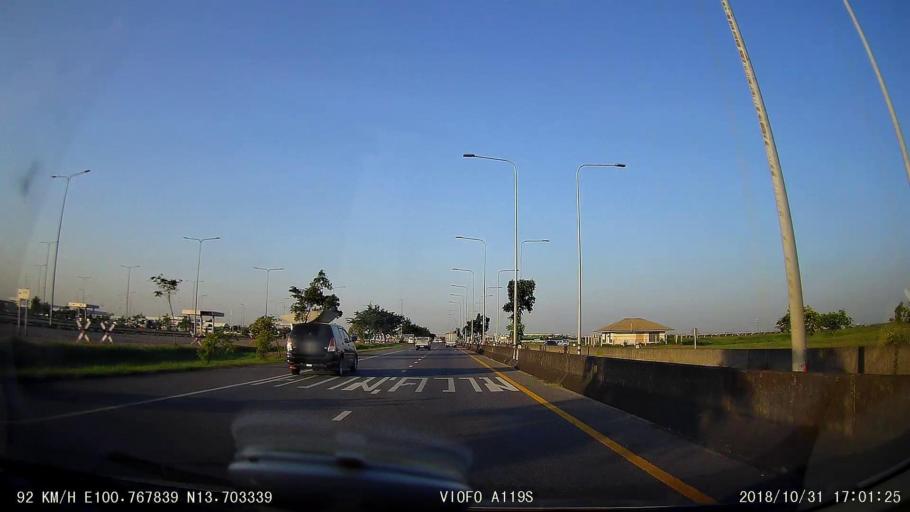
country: TH
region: Bangkok
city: Lat Krabang
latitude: 13.7034
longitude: 100.7679
